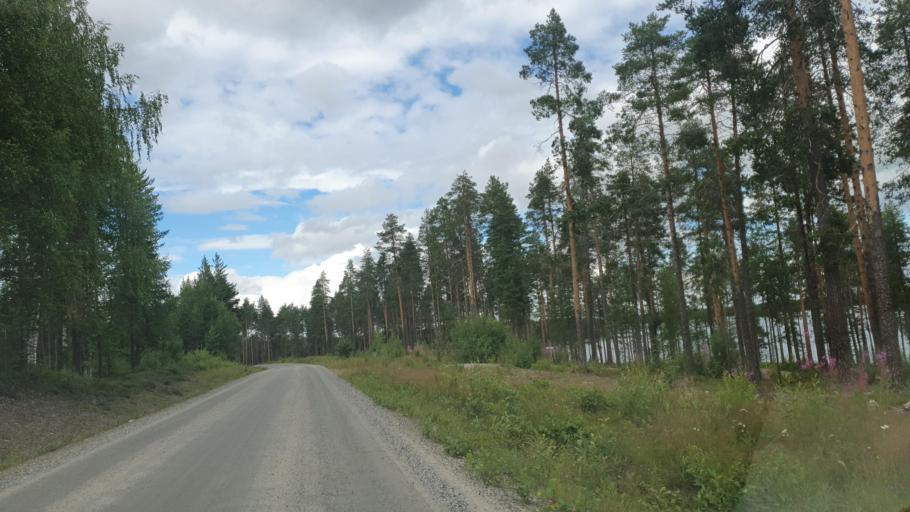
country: FI
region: Kainuu
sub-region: Kehys-Kainuu
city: Kuhmo
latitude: 64.0964
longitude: 29.4135
